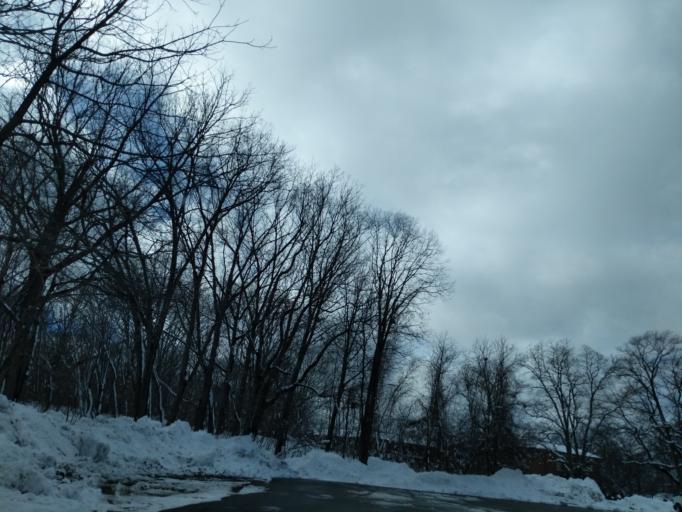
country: US
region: Massachusetts
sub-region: Worcester County
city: Worcester
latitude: 42.2853
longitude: -71.8095
